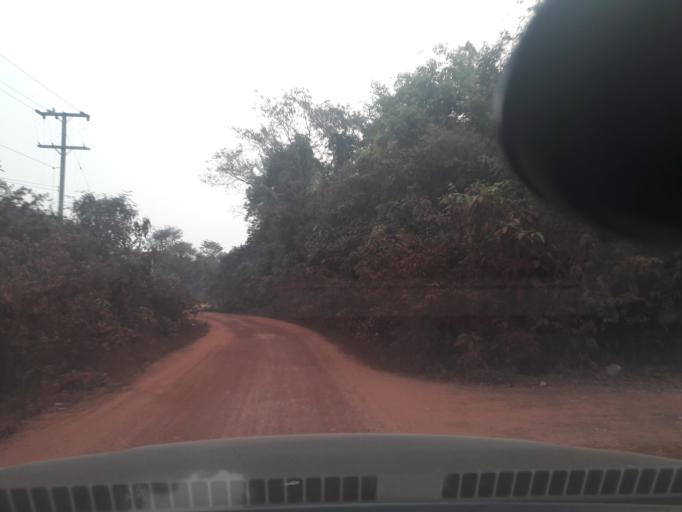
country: TH
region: Nong Khai
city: Si Chiang Mai
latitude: 18.0499
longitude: 102.4867
